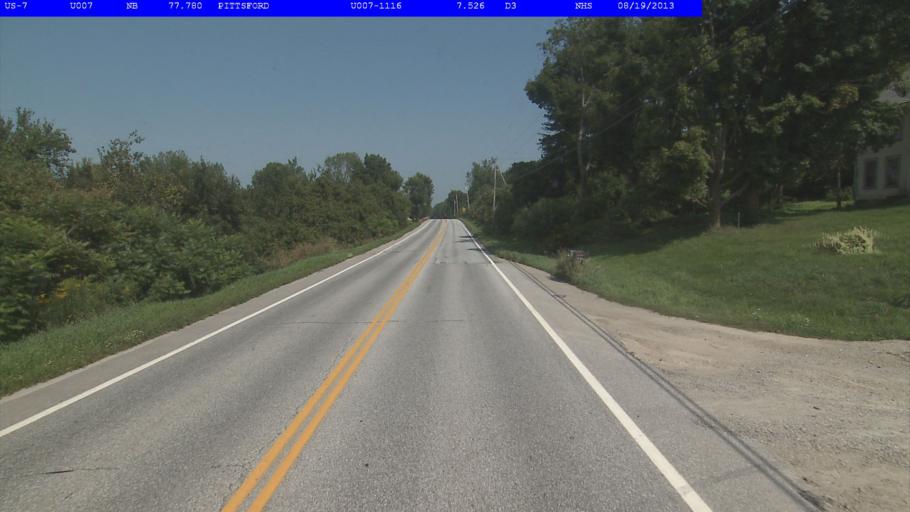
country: US
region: Vermont
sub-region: Rutland County
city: Brandon
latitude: 43.7533
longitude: -73.0480
